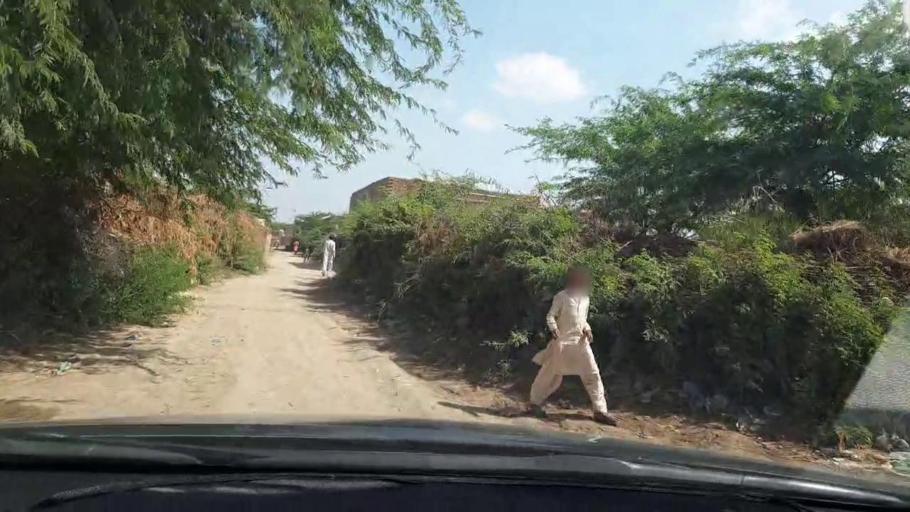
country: PK
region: Sindh
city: Naukot
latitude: 24.8772
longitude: 69.2558
